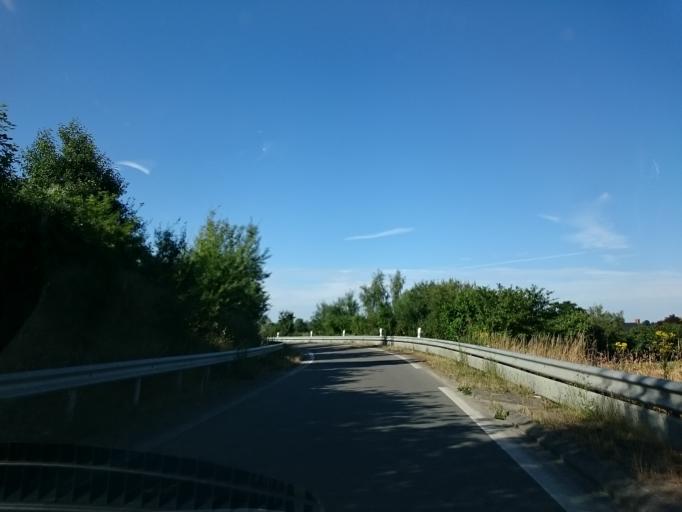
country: FR
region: Brittany
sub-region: Departement d'Ille-et-Vilaine
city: Corps-Nuds
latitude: 47.9901
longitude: -1.5884
